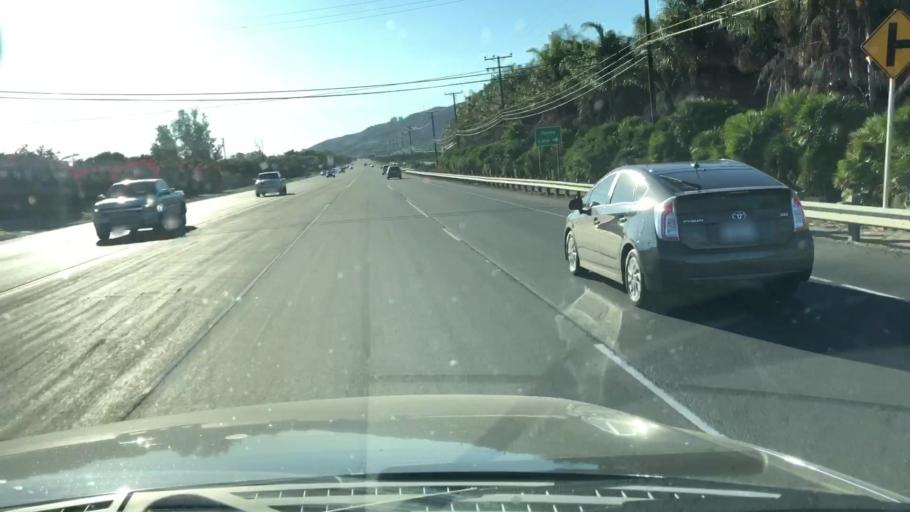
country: US
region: California
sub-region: Ventura County
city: Piru
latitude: 34.4007
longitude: -118.8140
